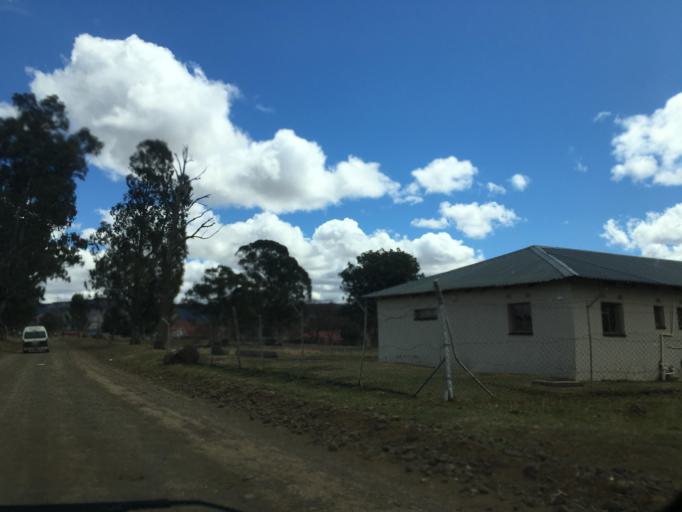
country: ZA
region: Eastern Cape
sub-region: Chris Hani District Municipality
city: Cala
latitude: -31.5280
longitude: 27.7016
